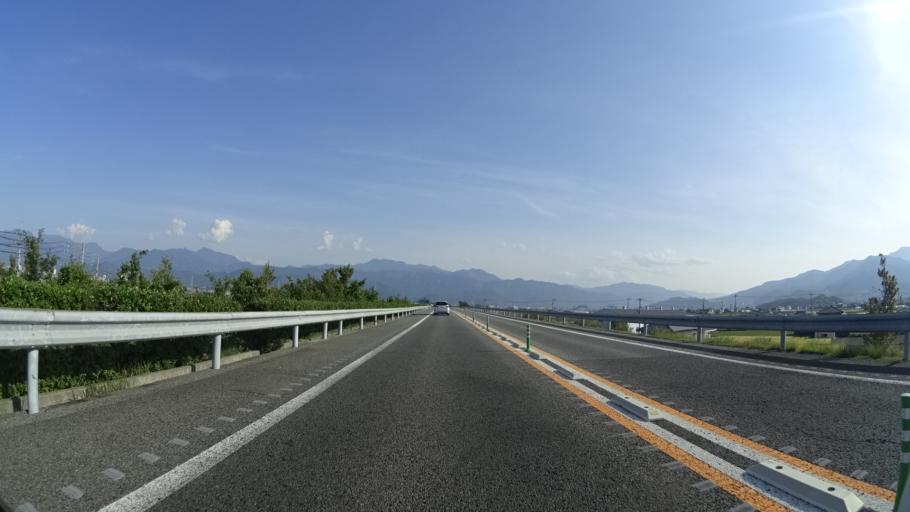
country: JP
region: Ehime
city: Saijo
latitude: 33.9398
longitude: 133.0692
